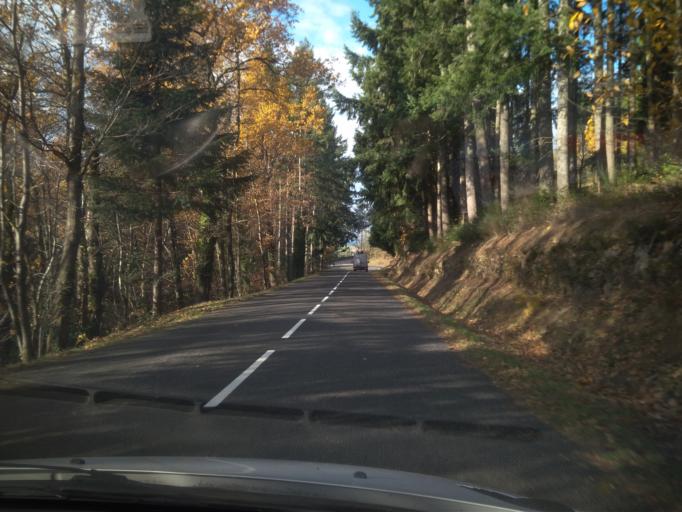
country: FR
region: Auvergne
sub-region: Departement de l'Allier
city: Le Mayet-de-Montagne
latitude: 46.1480
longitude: 3.7386
